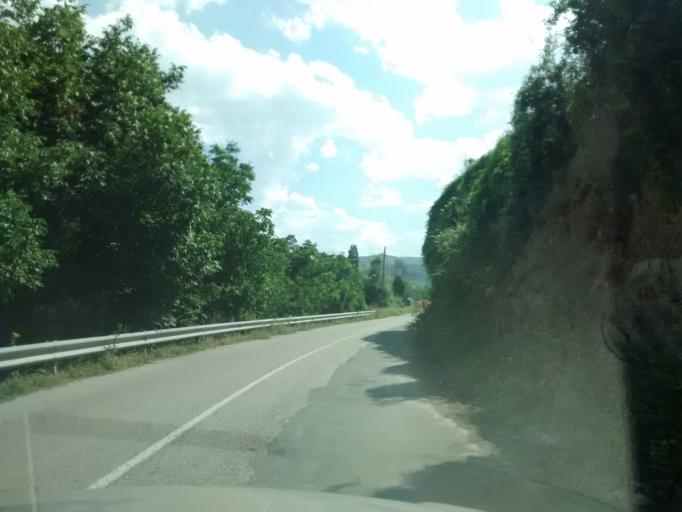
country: ES
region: La Rioja
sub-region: Provincia de La Rioja
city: San Roman de Cameros
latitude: 42.2326
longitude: -2.4724
